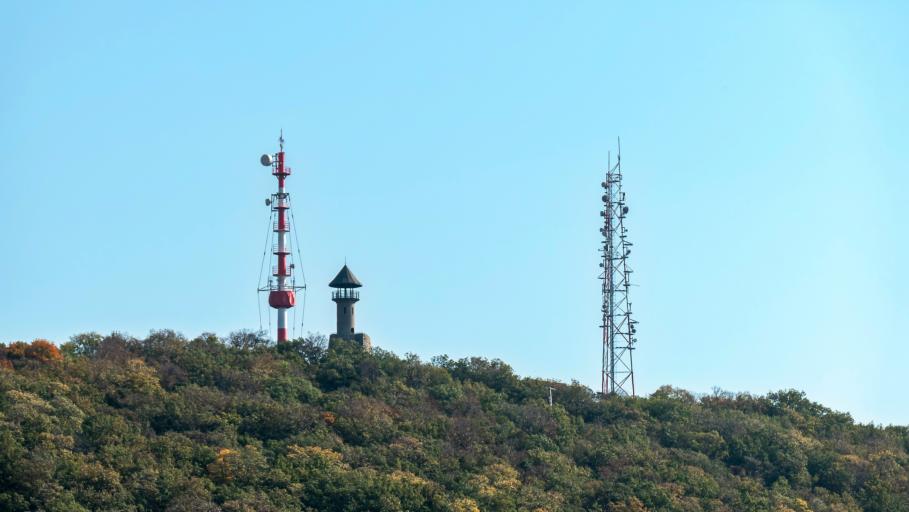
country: HU
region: Baranya
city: Pecs
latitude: 46.1098
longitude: 18.1921
